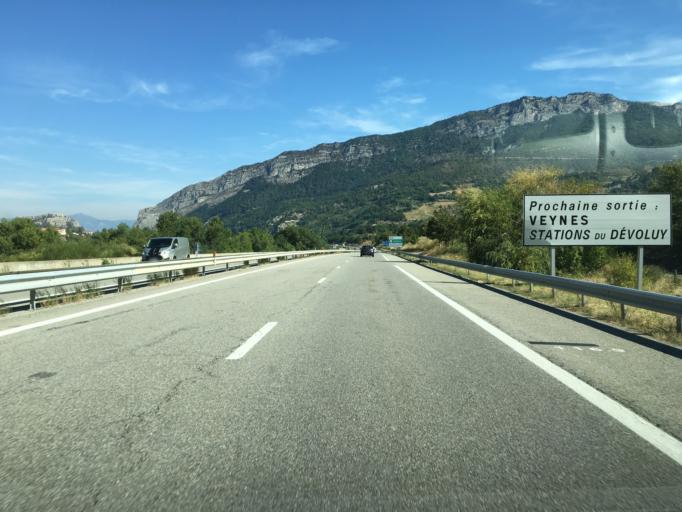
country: FR
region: Provence-Alpes-Cote d'Azur
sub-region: Departement des Alpes-de-Haute-Provence
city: Sisteron
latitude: 44.1754
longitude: 5.9540
